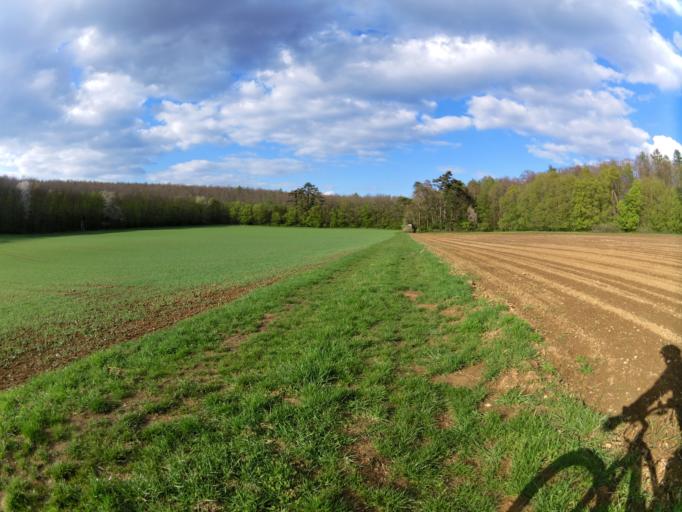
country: DE
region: Bavaria
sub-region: Regierungsbezirk Unterfranken
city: Greussenheim
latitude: 49.7864
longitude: 9.7816
